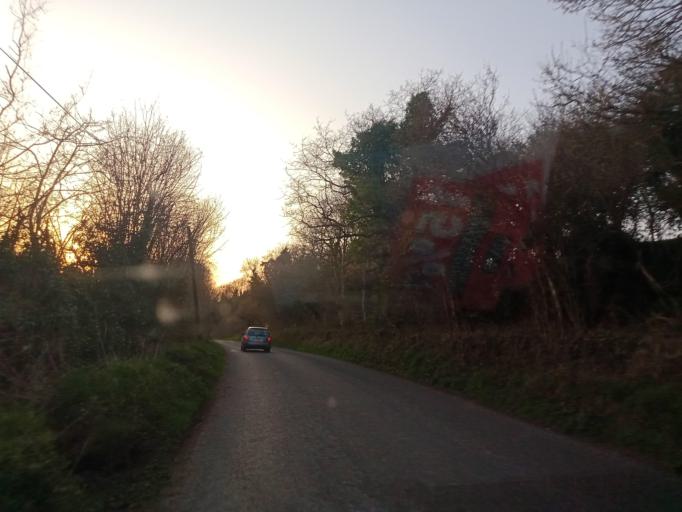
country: IE
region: Leinster
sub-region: Kilkenny
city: Castlecomer
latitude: 52.8631
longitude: -7.2704
